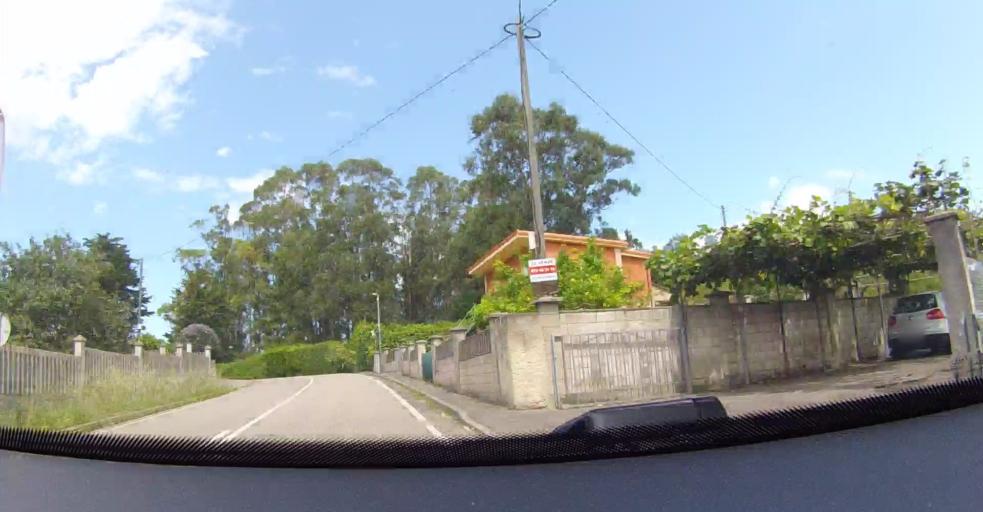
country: ES
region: Asturias
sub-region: Province of Asturias
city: Villaviciosa
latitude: 43.5300
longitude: -5.3731
